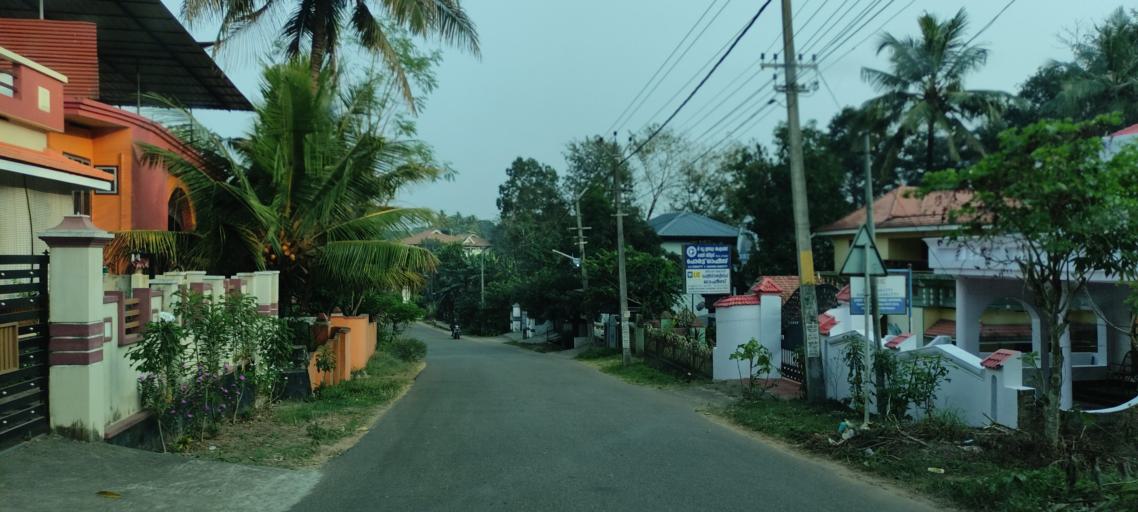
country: IN
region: Kerala
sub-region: Pattanamtitta
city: Adur
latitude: 9.0900
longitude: 76.7514
